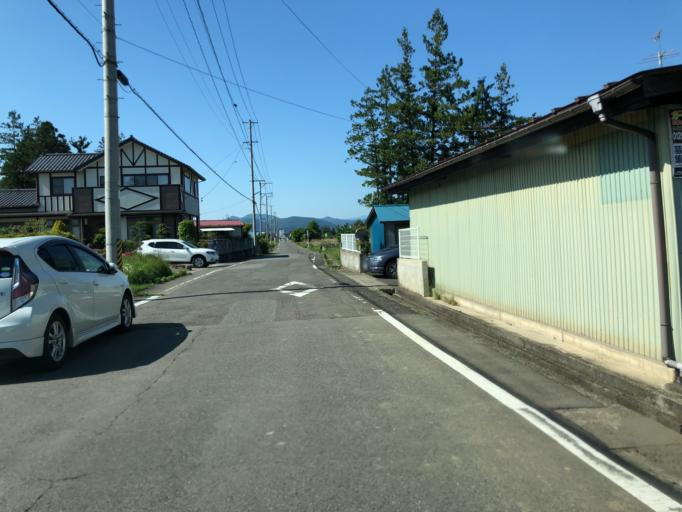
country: JP
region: Fukushima
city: Fukushima-shi
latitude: 37.7318
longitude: 140.4087
